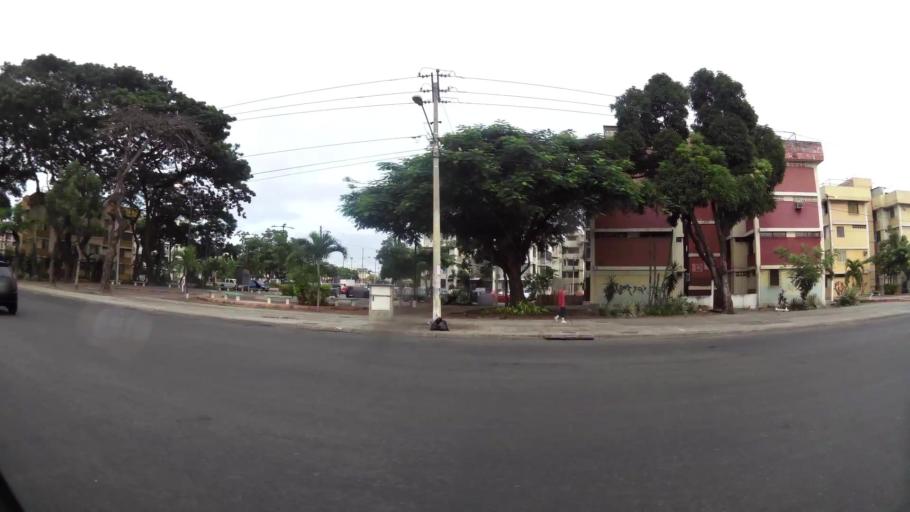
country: EC
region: Guayas
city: Guayaquil
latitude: -2.2233
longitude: -79.8987
